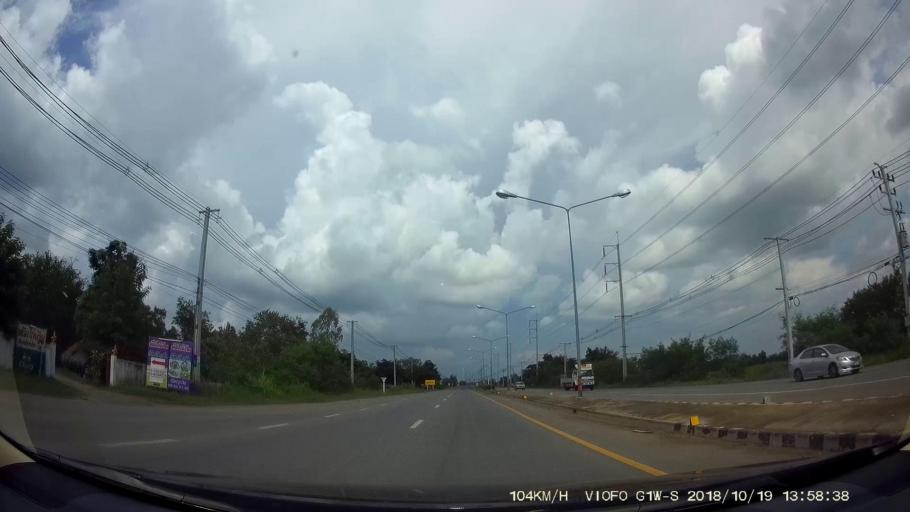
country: TH
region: Chaiyaphum
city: Chaiyaphum
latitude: 15.7999
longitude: 102.0561
